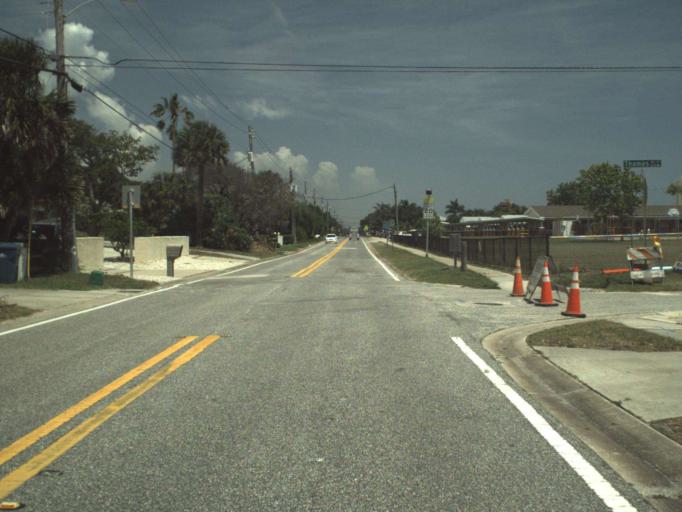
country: US
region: Florida
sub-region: Volusia County
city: Daytona Beach Shores
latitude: 29.1748
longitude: -80.9860
